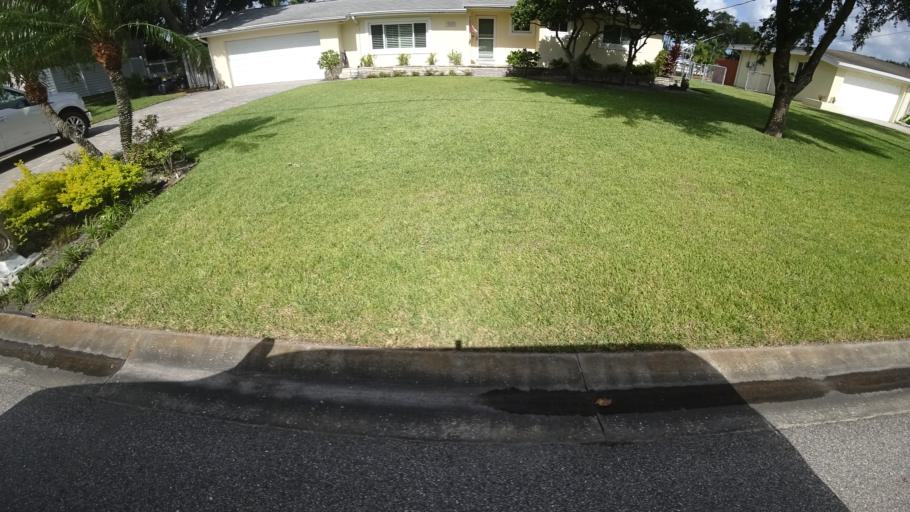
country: US
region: Florida
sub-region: Manatee County
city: Memphis
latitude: 27.5604
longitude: -82.5686
